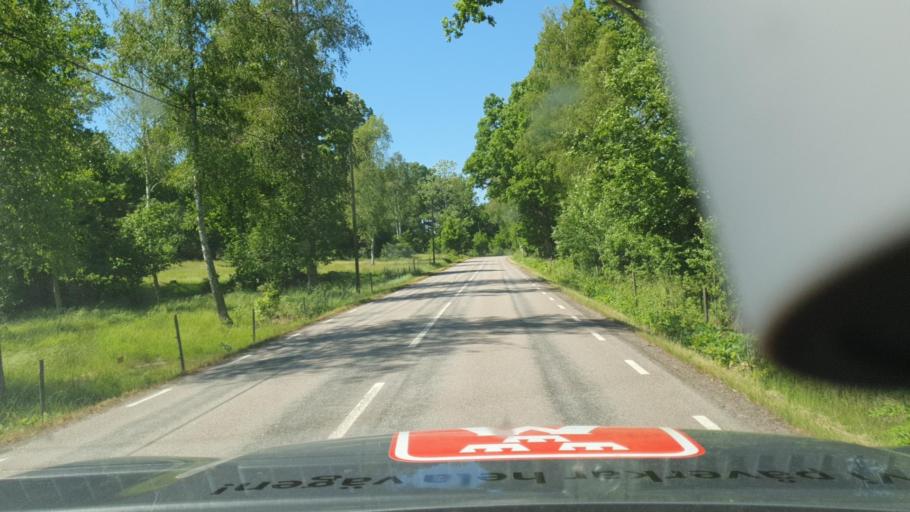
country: SE
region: Kalmar
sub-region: Torsas Kommun
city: Torsas
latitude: 56.4817
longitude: 15.7553
